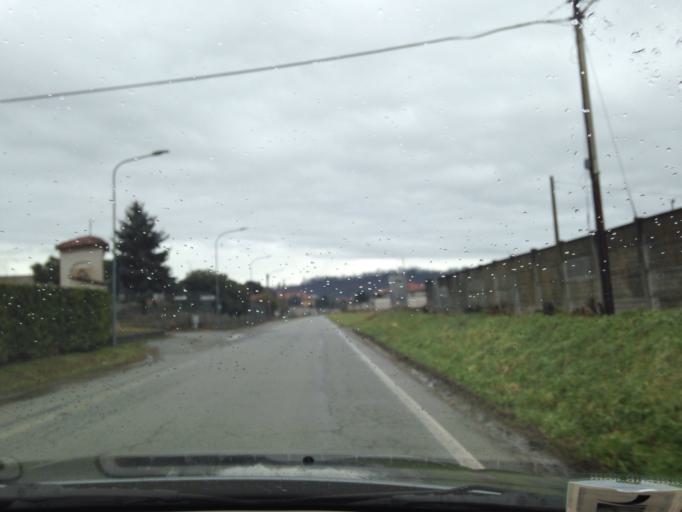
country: IT
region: Piedmont
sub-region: Provincia di Torino
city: Villareggia
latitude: 45.3049
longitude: 7.9780
